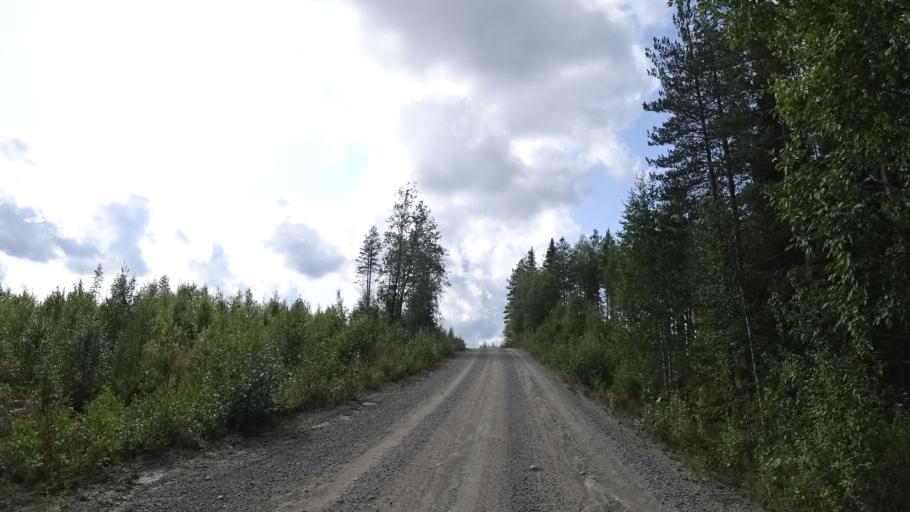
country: FI
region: North Karelia
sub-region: Joensuu
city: Ilomantsi
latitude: 62.9264
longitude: 31.3638
